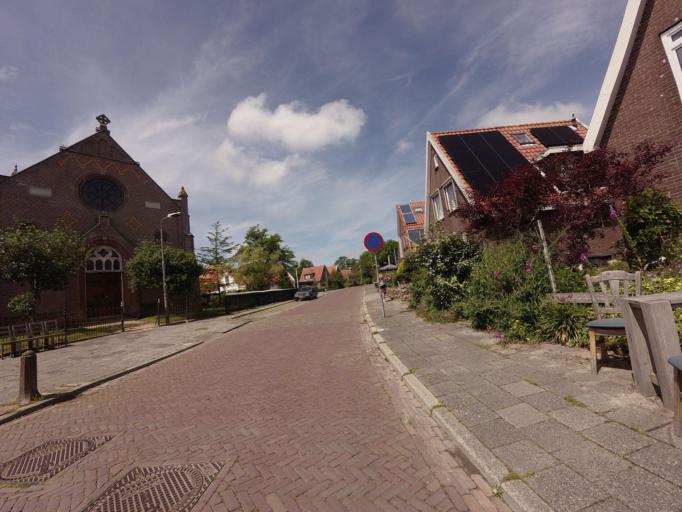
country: NL
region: North Holland
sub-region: Gemeente Texel
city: Den Burg
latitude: 53.0848
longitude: 4.8719
